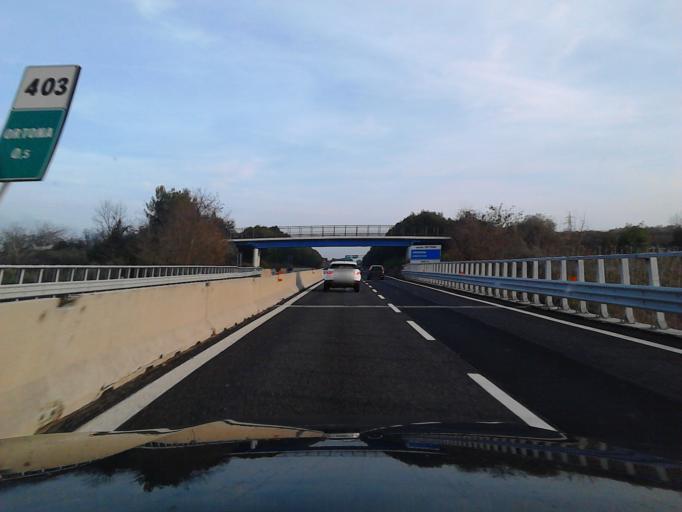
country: IT
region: Abruzzo
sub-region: Provincia di Chieti
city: Ortona
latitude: 42.3335
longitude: 14.3730
